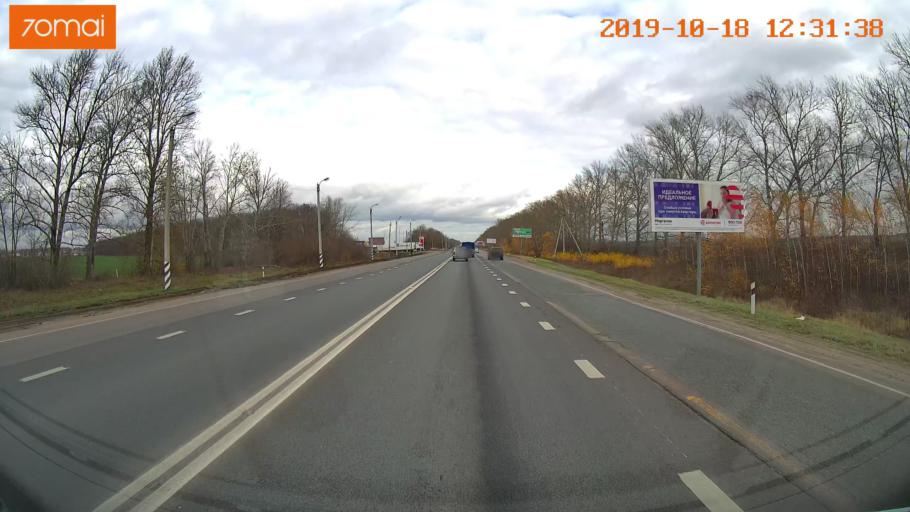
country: RU
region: Rjazan
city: Ryazan'
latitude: 54.5947
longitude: 39.6145
